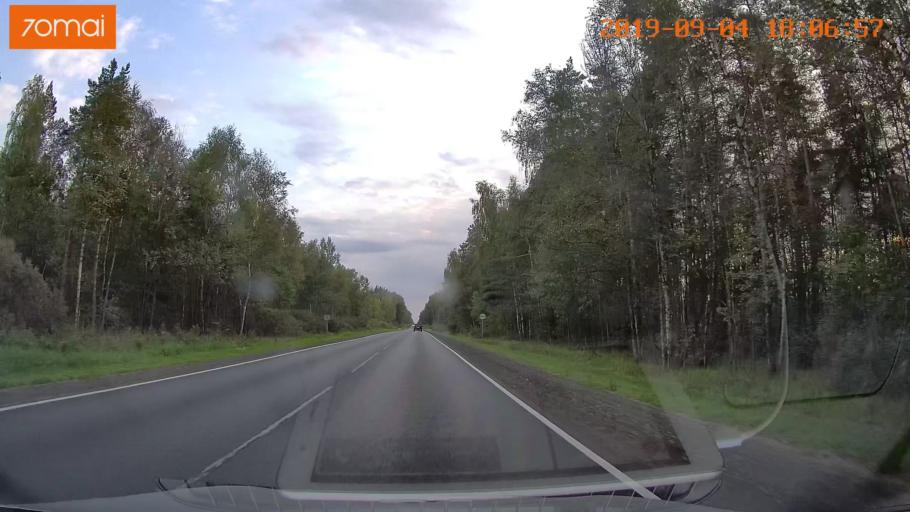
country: RU
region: Moskovskaya
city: Khorlovo
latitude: 55.4254
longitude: 38.8081
